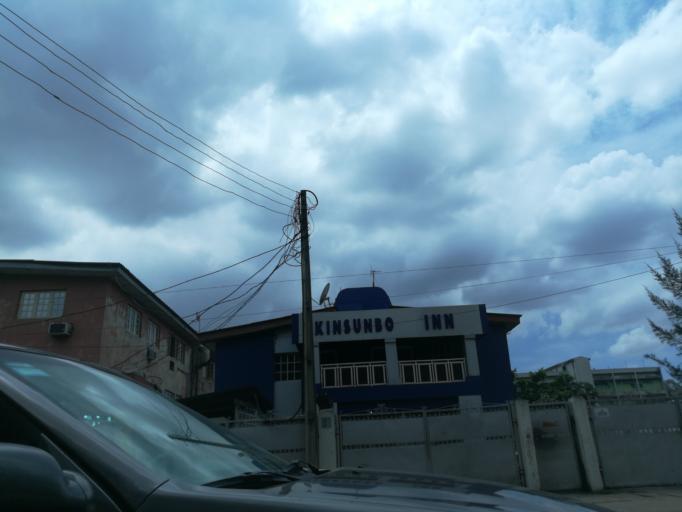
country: NG
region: Lagos
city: Ikeja
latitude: 6.5962
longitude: 3.3505
